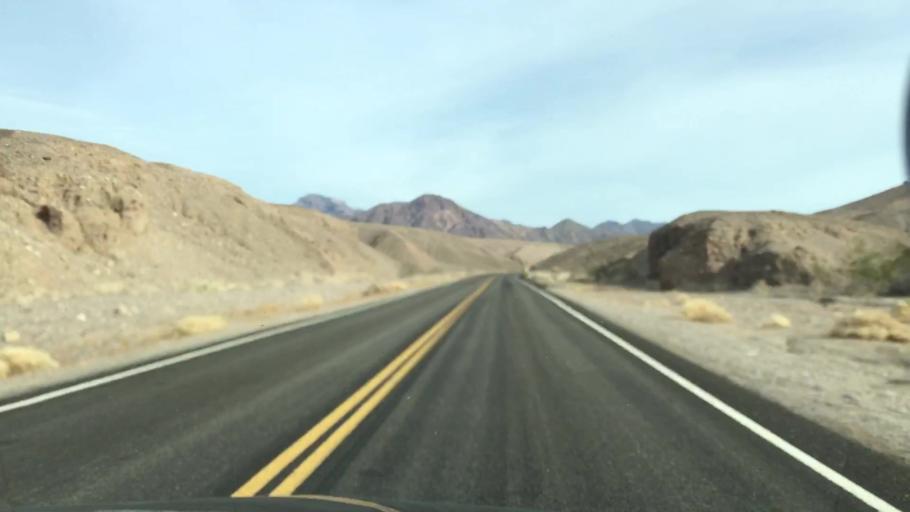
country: US
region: Nevada
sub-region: Nye County
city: Beatty
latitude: 36.6635
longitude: -117.0187
